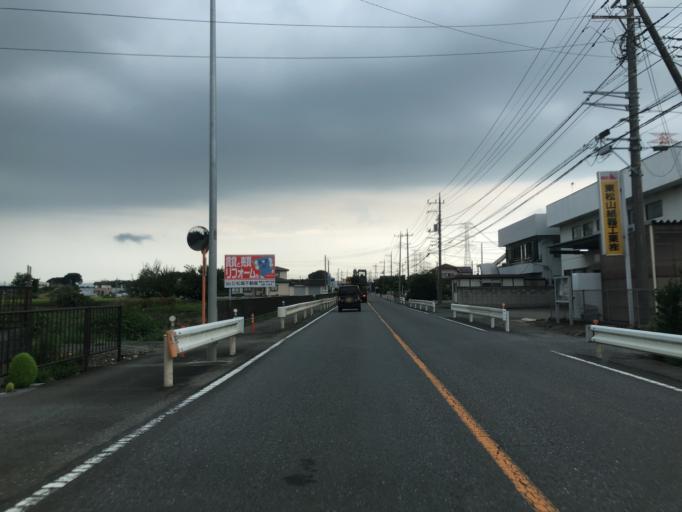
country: JP
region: Saitama
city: Sakado
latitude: 36.0238
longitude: 139.3944
